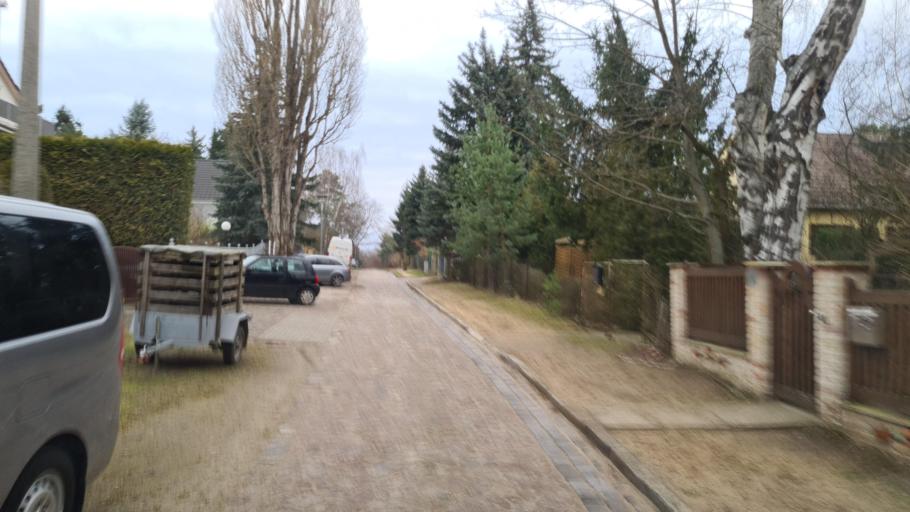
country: DE
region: Brandenburg
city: Stahnsdorf
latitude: 52.3903
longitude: 13.2031
